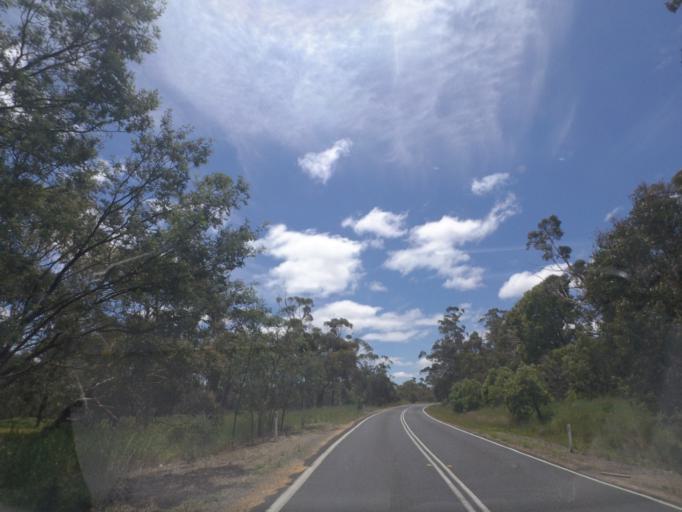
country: AU
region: Victoria
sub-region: Mount Alexander
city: Castlemaine
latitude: -37.3223
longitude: 144.1626
